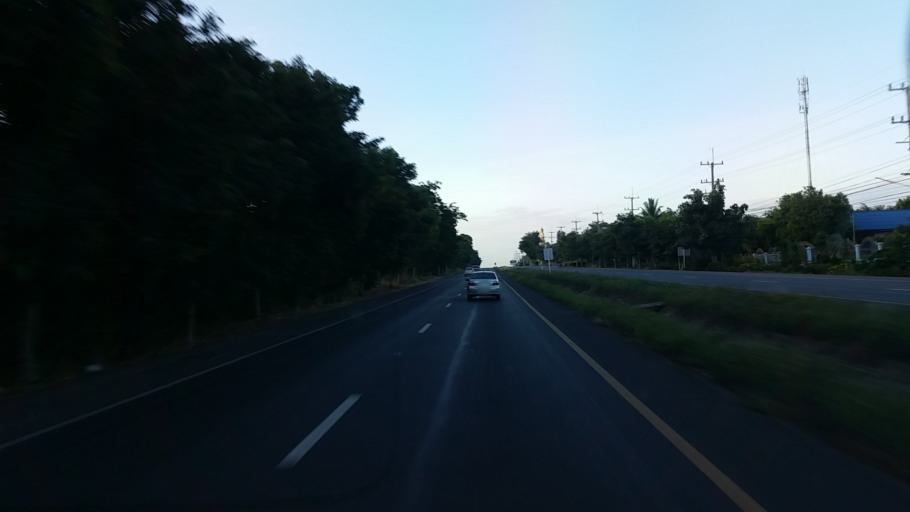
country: TH
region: Lop Buri
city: Chai Badan
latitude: 15.1603
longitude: 101.0591
